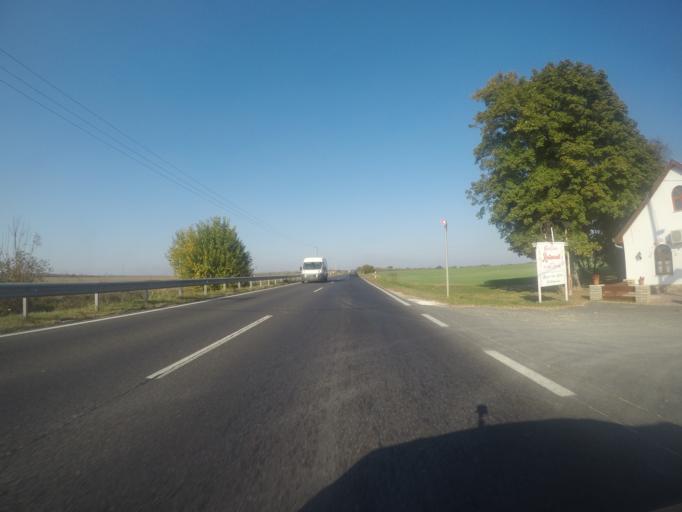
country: HU
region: Tolna
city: Dunafoldvar
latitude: 46.8430
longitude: 18.9103
